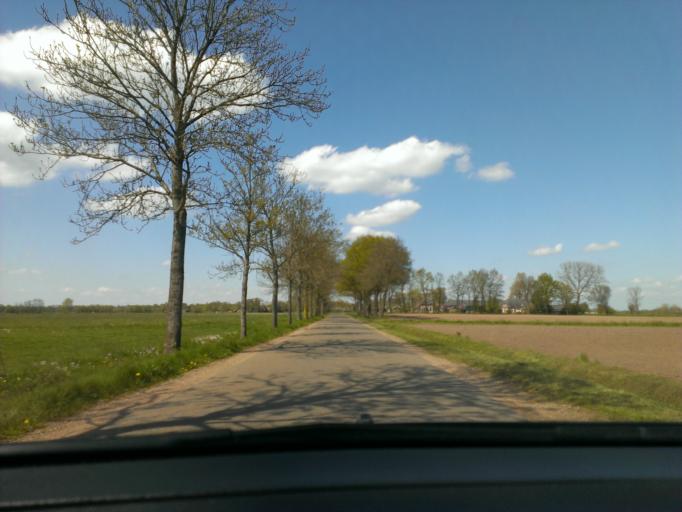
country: NL
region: Gelderland
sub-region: Gemeente Epe
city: Oene
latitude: 52.3561
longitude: 6.0535
